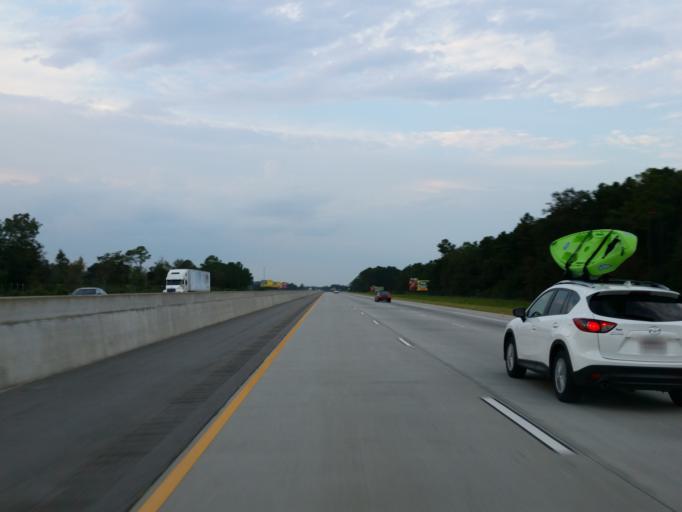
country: US
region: Georgia
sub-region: Tift County
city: Omega
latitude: 31.2966
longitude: -83.4772
